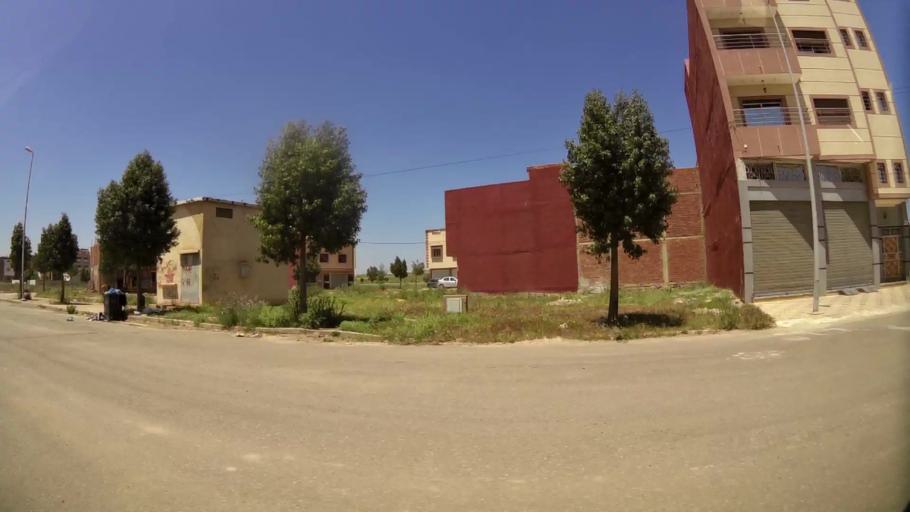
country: MA
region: Oriental
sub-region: Oujda-Angad
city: Oujda
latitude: 34.6650
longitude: -1.9482
